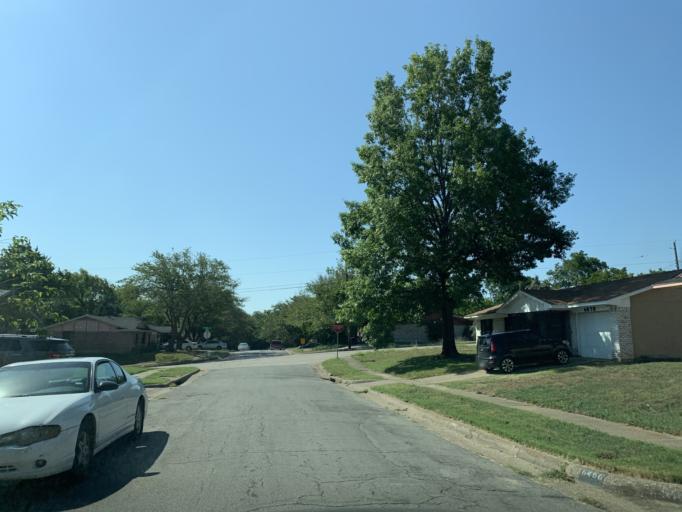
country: US
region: Texas
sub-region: Dallas County
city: Hutchins
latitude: 32.6673
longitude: -96.7522
